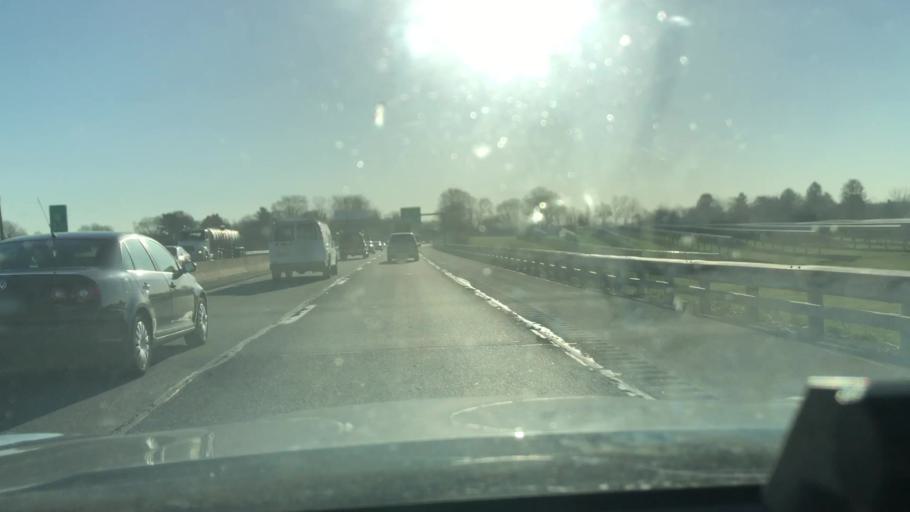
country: US
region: Pennsylvania
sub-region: Northampton County
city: Middletown
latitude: 40.6828
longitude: -75.3125
